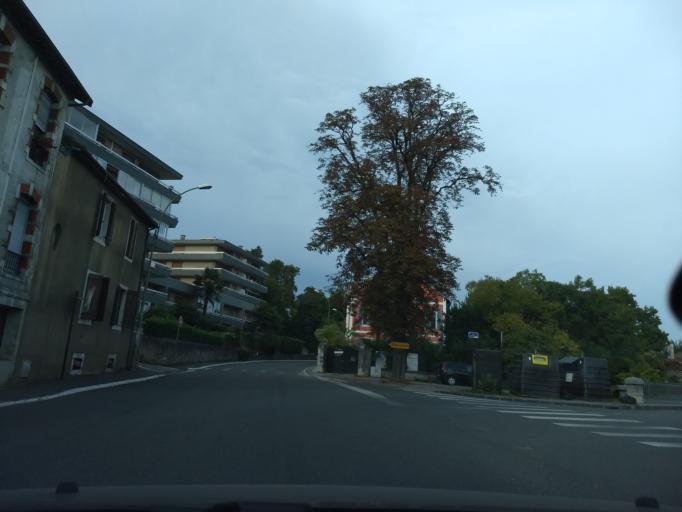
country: FR
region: Aquitaine
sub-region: Departement des Pyrenees-Atlantiques
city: Pau
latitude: 43.2932
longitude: -0.3613
